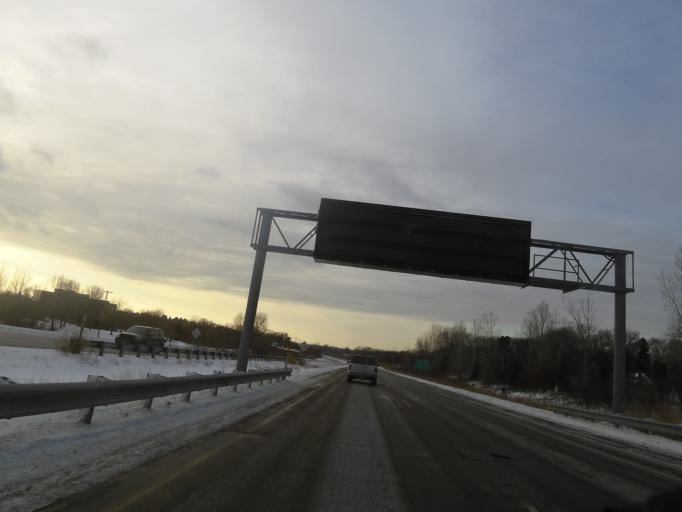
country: US
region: Minnesota
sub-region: Dakota County
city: Mendota Heights
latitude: 44.8838
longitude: -93.1497
